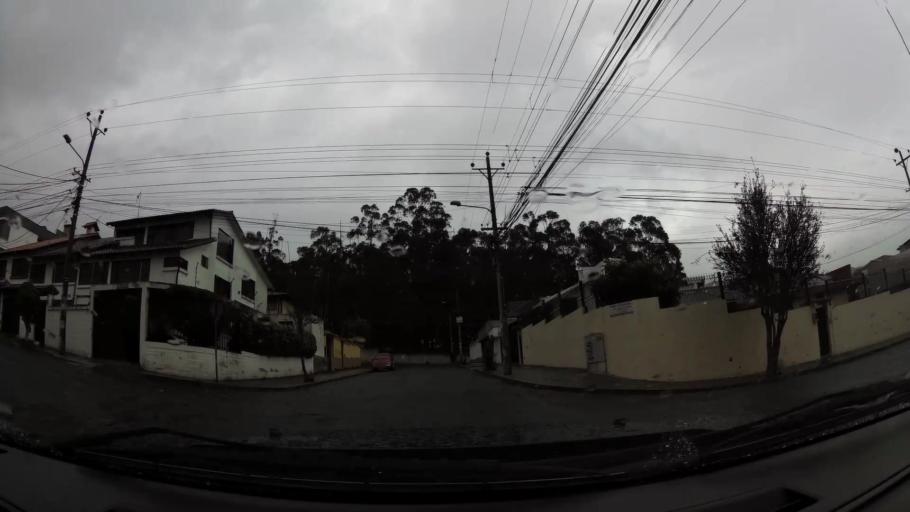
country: EC
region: Pichincha
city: Quito
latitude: -0.1098
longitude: -78.5004
